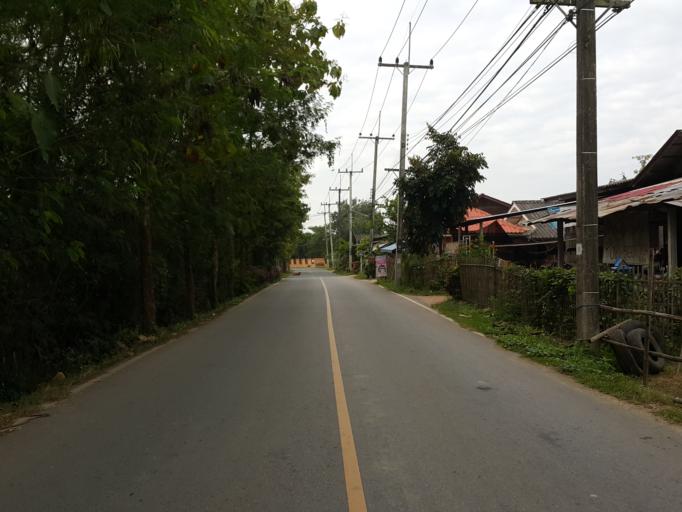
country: TH
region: Chiang Mai
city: San Kamphaeng
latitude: 18.7644
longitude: 99.1064
